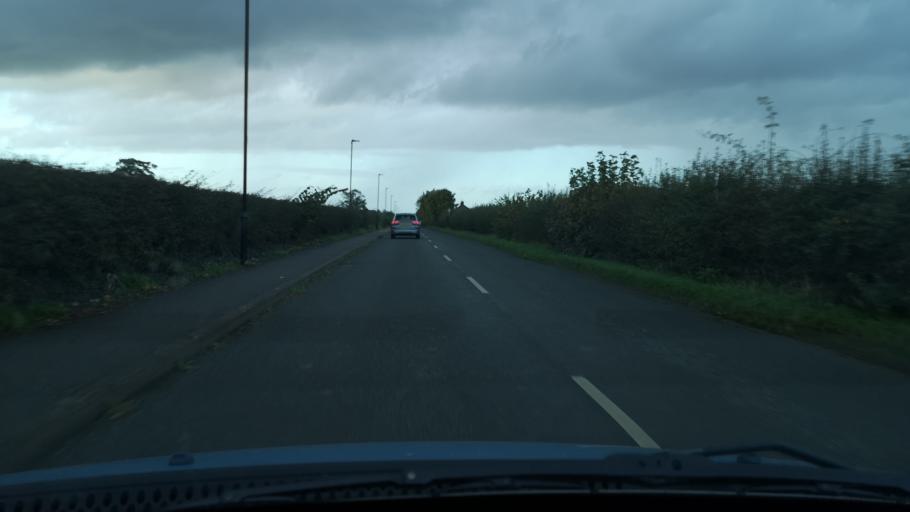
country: GB
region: England
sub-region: Doncaster
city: Norton
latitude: 53.6282
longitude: -1.1831
